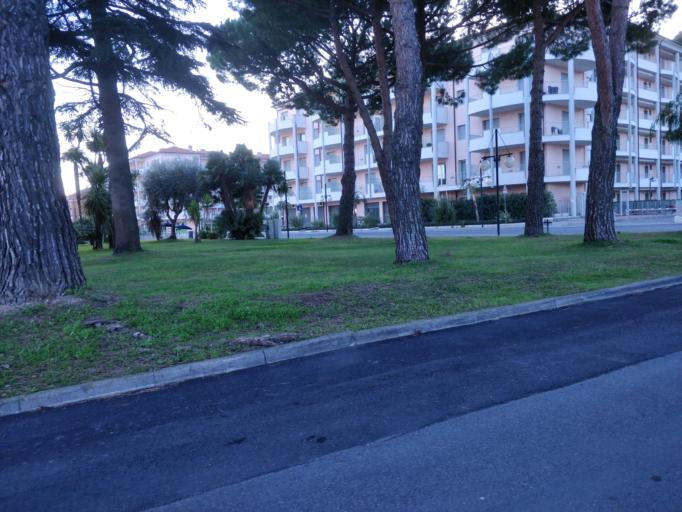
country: IT
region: Liguria
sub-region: Provincia di Savona
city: Andora
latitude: 43.9587
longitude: 8.1398
